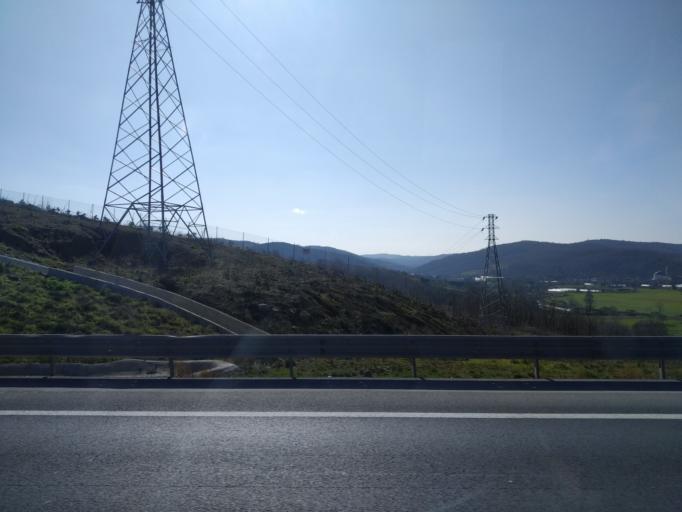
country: TR
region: Istanbul
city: Mahmut Sevket Pasa
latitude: 41.1863
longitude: 29.2160
